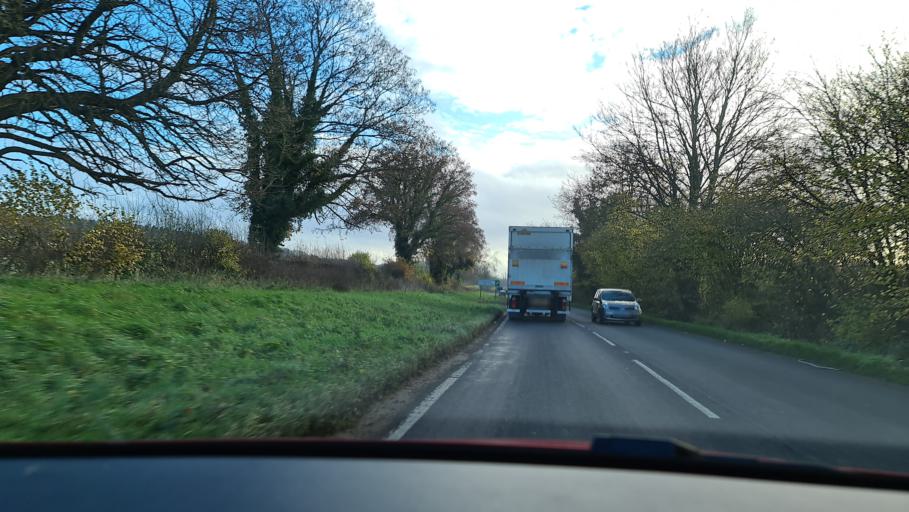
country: GB
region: England
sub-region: Buckinghamshire
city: Great Missenden
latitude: 51.6852
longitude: -0.6818
